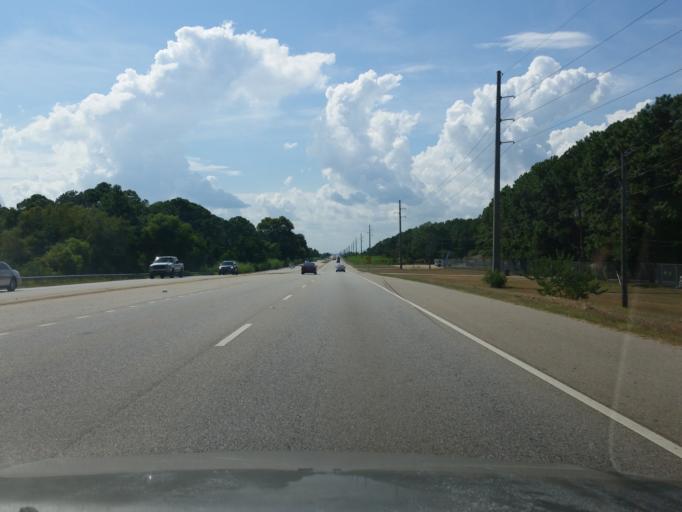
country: US
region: Alabama
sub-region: Baldwin County
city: Spanish Fort
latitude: 30.6686
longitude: -87.9280
